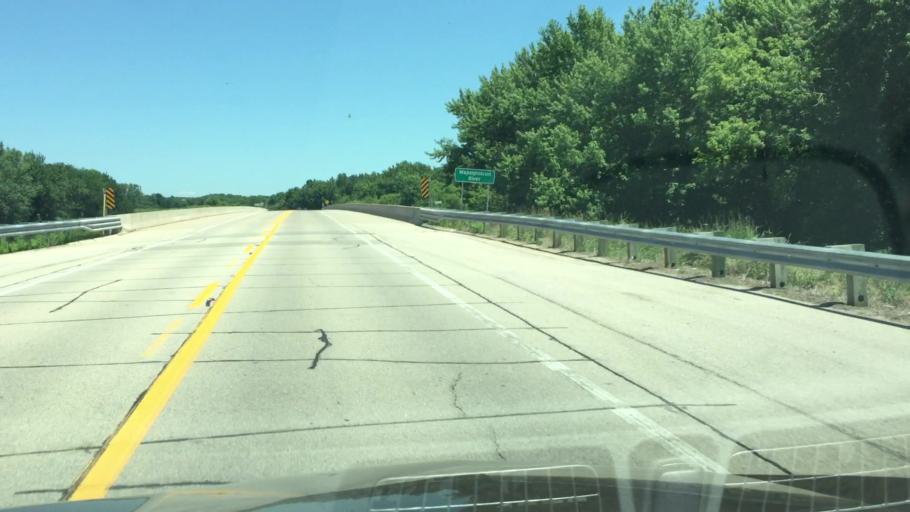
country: US
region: Iowa
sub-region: Cedar County
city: Mechanicsville
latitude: 42.0077
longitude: -91.1407
